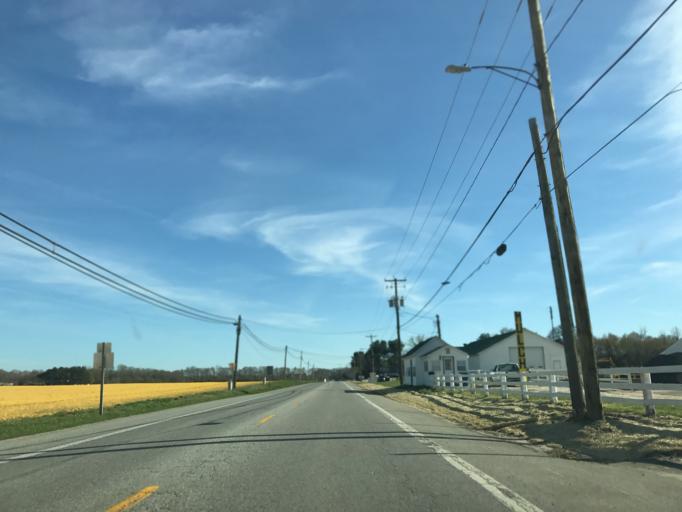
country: US
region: Maryland
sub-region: Caroline County
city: Greensboro
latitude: 39.0313
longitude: -75.7870
